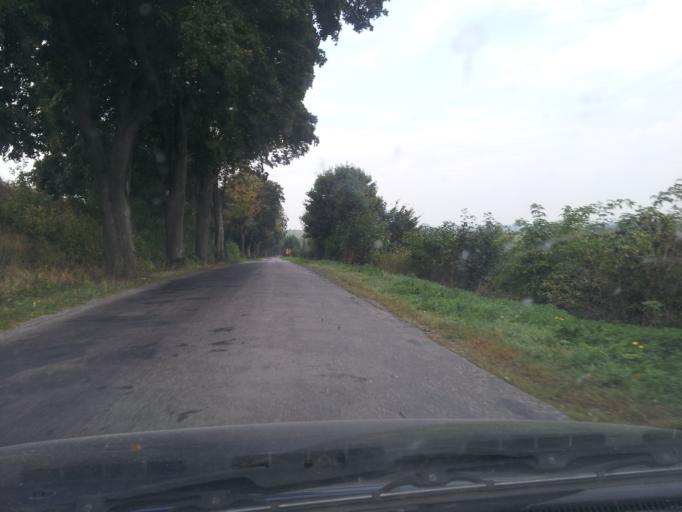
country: PL
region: Warmian-Masurian Voivodeship
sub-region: Powiat nowomiejski
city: Nowe Miasto Lubawskie
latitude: 53.3981
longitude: 19.6225
